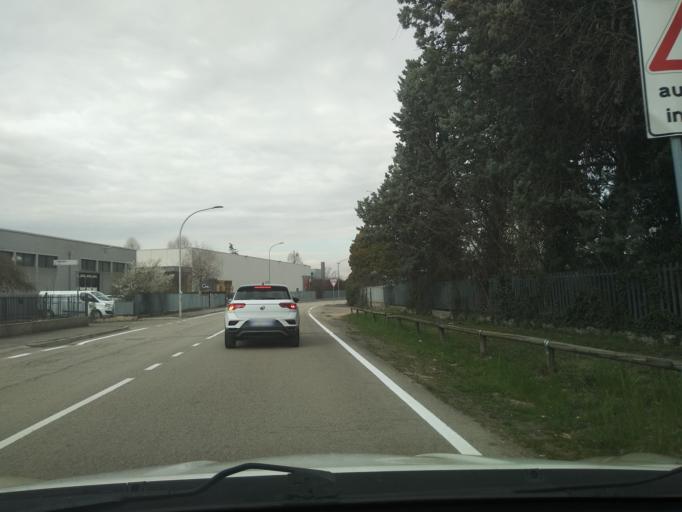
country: IT
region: Veneto
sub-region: Provincia di Padova
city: Rubano
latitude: 45.4247
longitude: 11.7914
